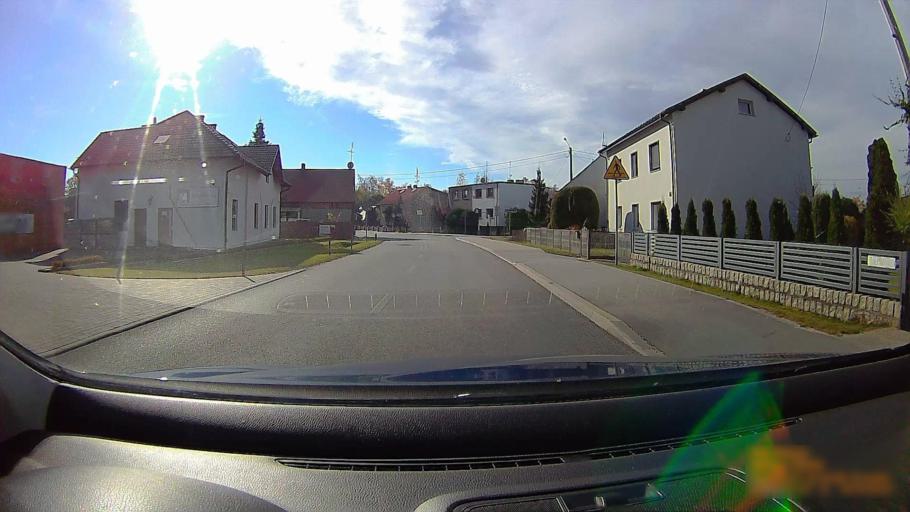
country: PL
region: Greater Poland Voivodeship
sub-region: Powiat ostrzeszowski
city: Doruchow
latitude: 51.3643
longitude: 18.0287
